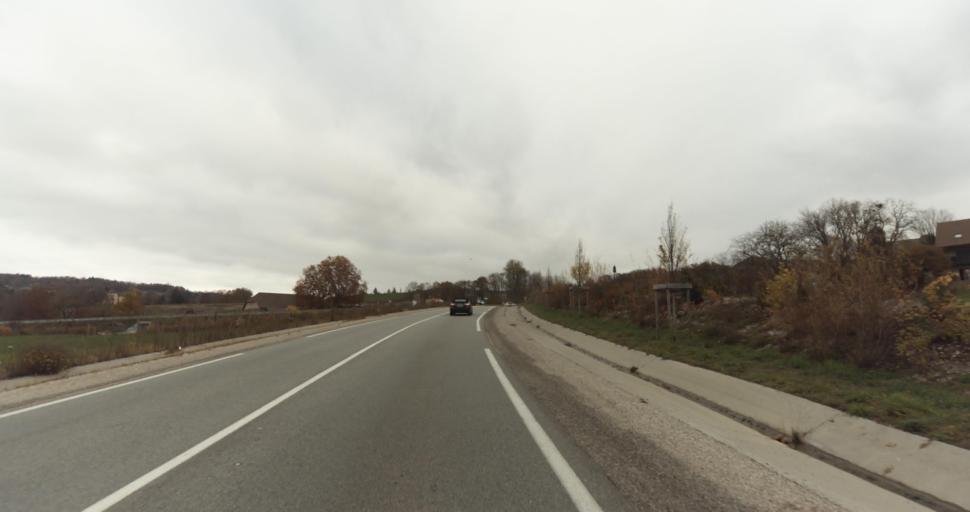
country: FR
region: Rhone-Alpes
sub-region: Departement de la Haute-Savoie
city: Pringy
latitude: 45.9489
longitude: 6.1219
